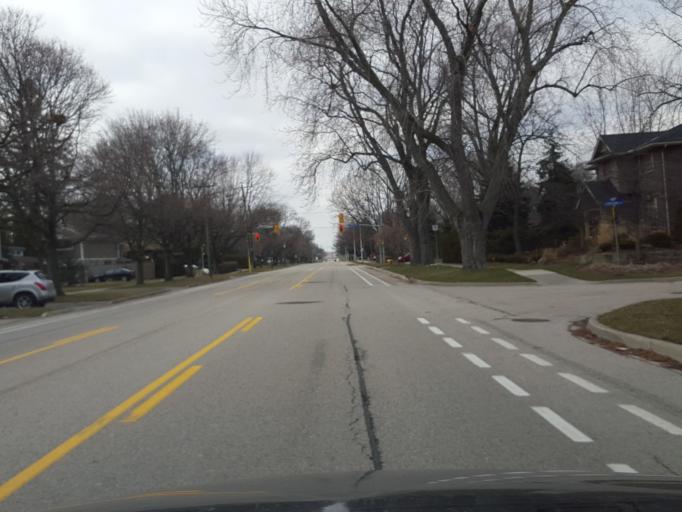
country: CA
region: Ontario
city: Burlington
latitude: 43.3487
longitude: -79.7639
